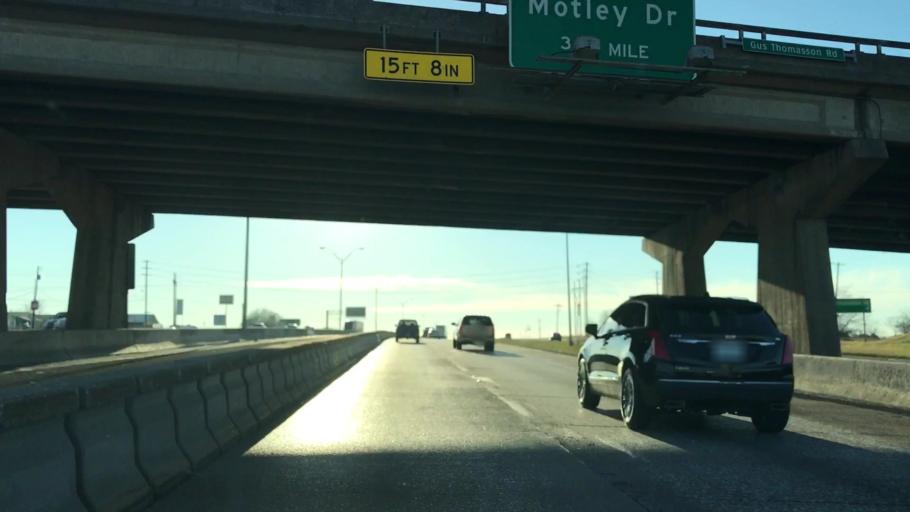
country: US
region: Texas
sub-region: Dallas County
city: Mesquite
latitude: 32.8177
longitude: -96.6391
